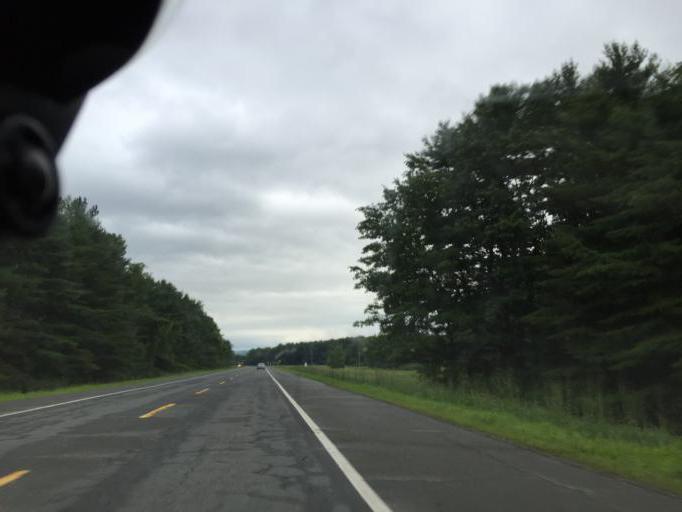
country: US
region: Connecticut
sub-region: Litchfield County
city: Canaan
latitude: 42.0601
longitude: -73.3275
